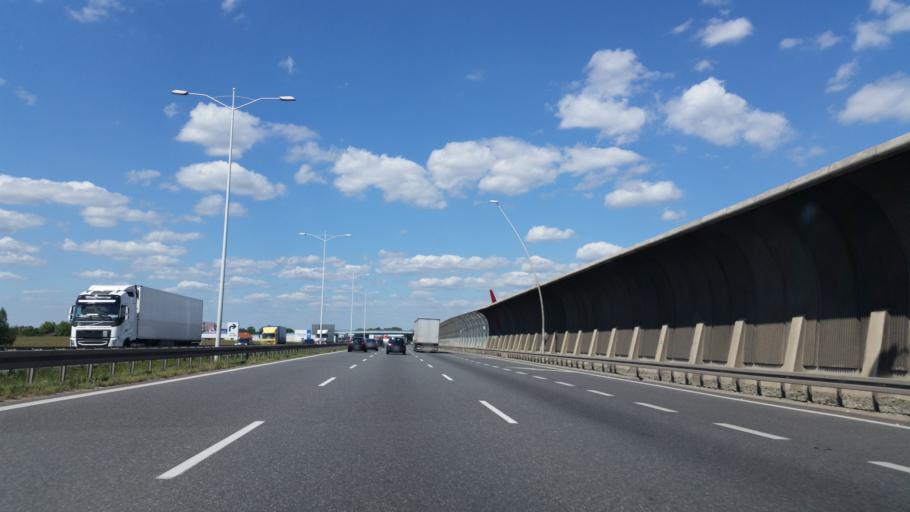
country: PL
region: Lower Silesian Voivodeship
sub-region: Powiat wroclawski
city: Smolec
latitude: 51.0695
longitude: 16.9282
